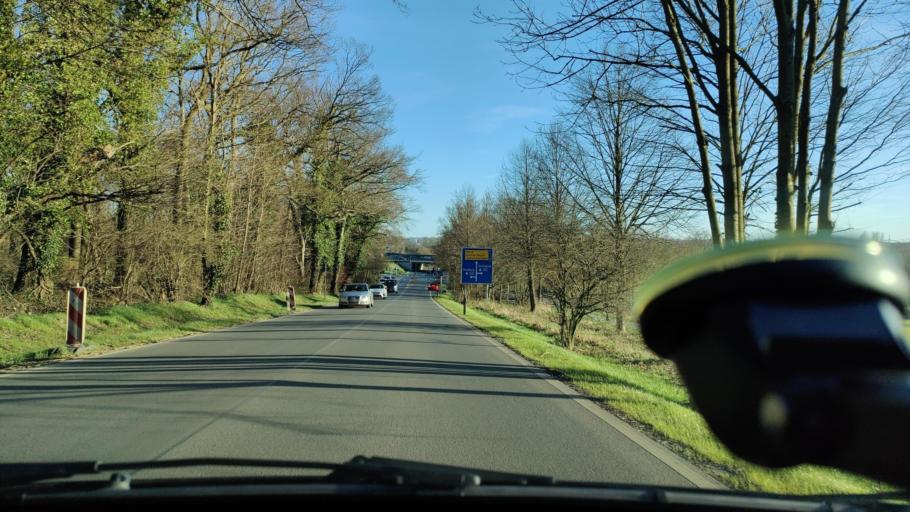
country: DE
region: North Rhine-Westphalia
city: Castrop-Rauxel
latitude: 51.5613
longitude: 7.2894
